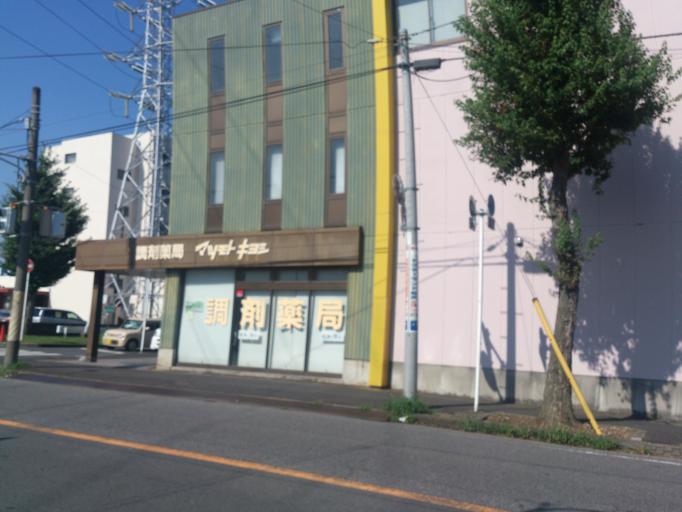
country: JP
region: Chiba
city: Matsudo
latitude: 35.7947
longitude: 139.9182
